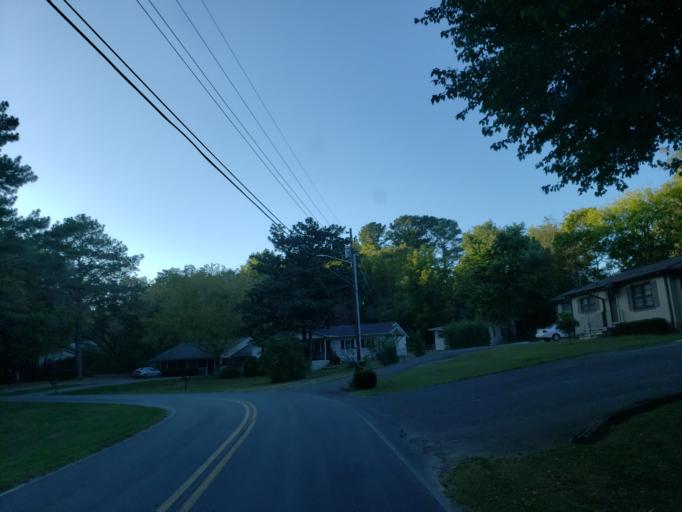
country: US
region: Georgia
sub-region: Pickens County
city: Jasper
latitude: 34.4619
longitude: -84.4246
